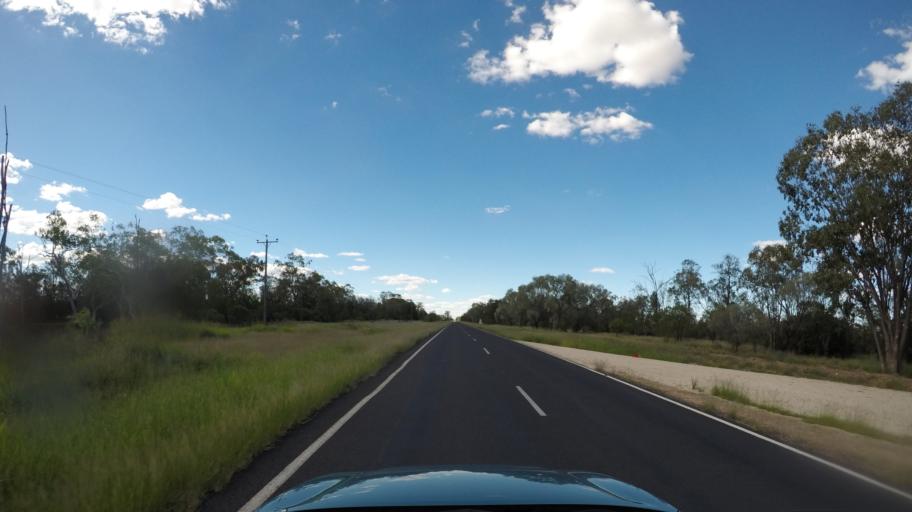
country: AU
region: Queensland
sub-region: Goondiwindi
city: Goondiwindi
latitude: -28.1654
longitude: 150.2867
